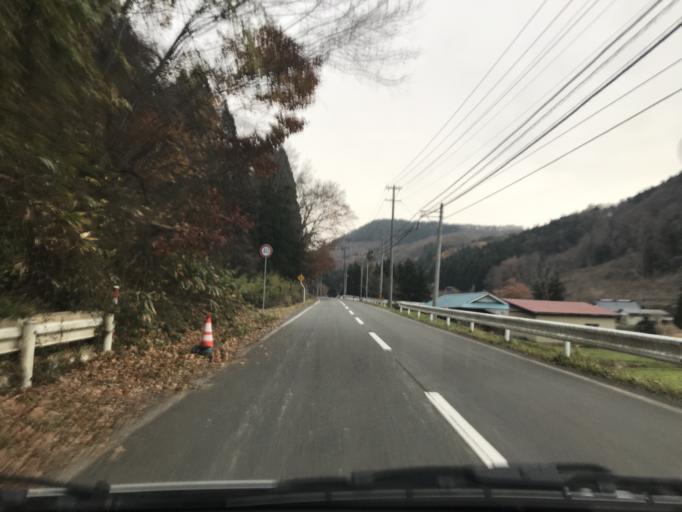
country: JP
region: Iwate
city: Tono
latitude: 39.1926
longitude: 141.3500
